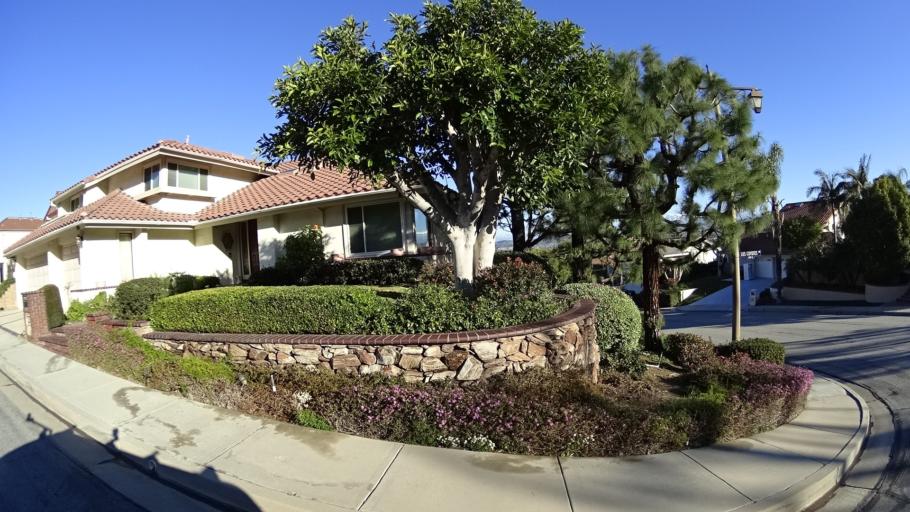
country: US
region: California
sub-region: Orange County
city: Villa Park
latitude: 33.8402
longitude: -117.7933
